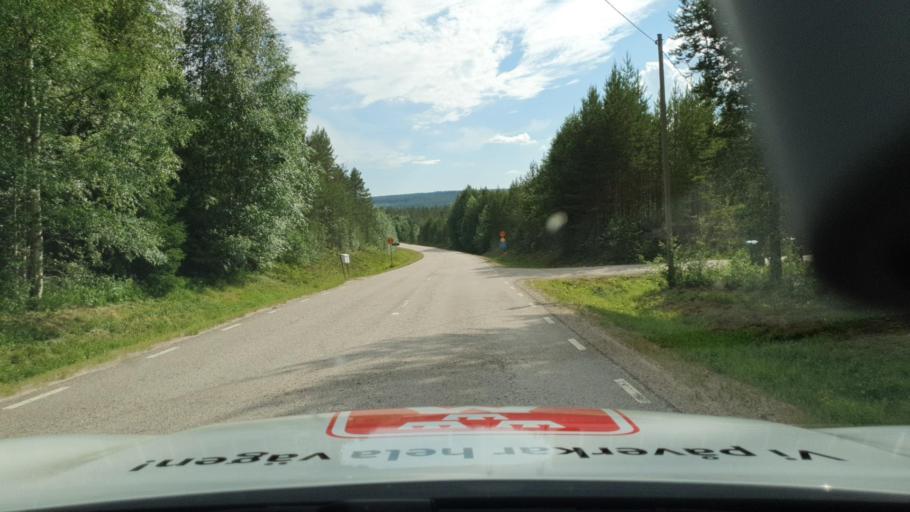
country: NO
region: Hedmark
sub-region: Trysil
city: Innbygda
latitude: 60.9605
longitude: 12.4734
